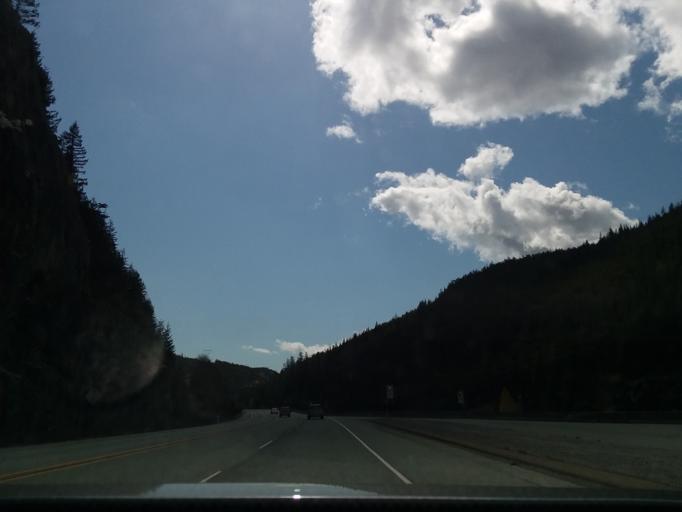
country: CA
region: British Columbia
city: Whistler
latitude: 49.9373
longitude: -123.1664
